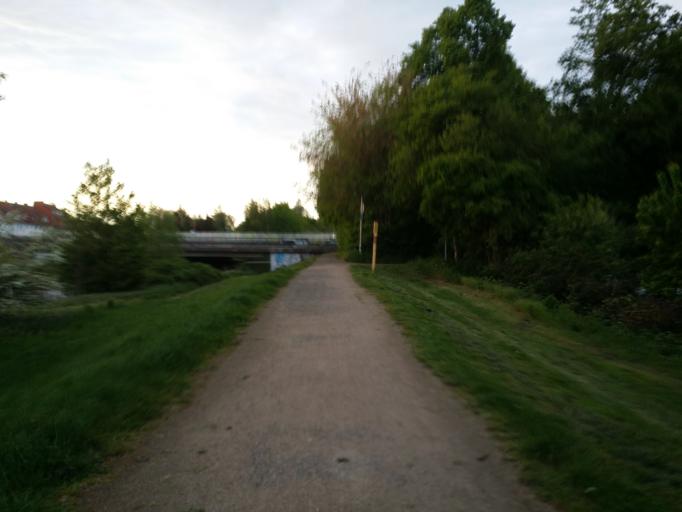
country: DE
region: Lower Saxony
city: Stuhr
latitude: 53.0601
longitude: 8.7693
